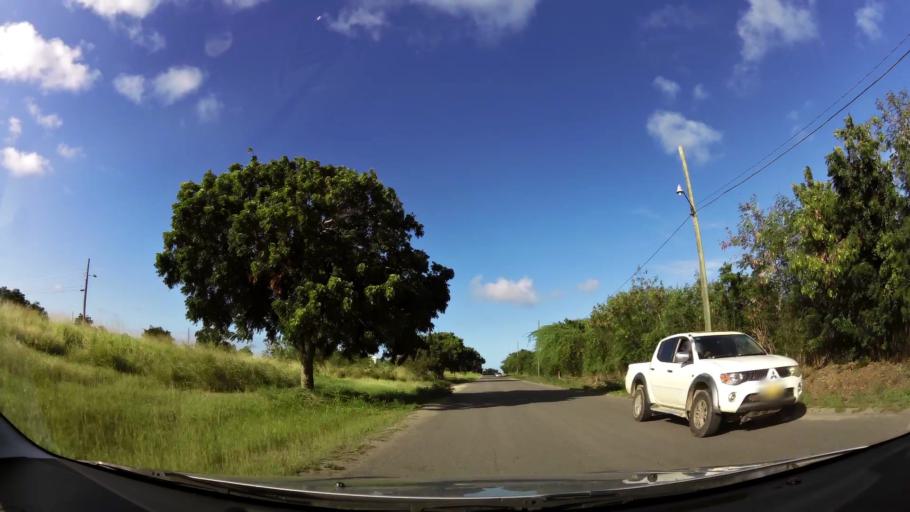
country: AG
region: Saint George
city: Piggotts
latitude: 17.1055
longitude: -61.8003
